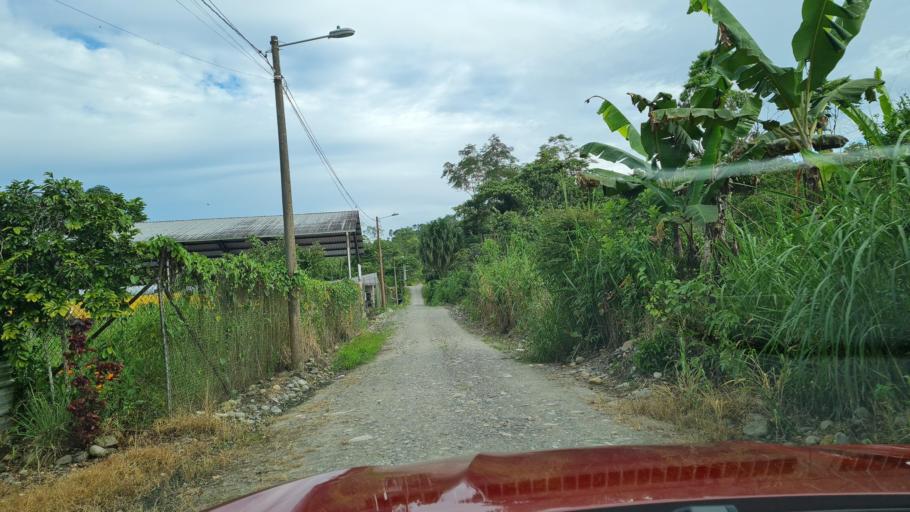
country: EC
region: Napo
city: Tena
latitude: -1.0460
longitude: -77.7778
